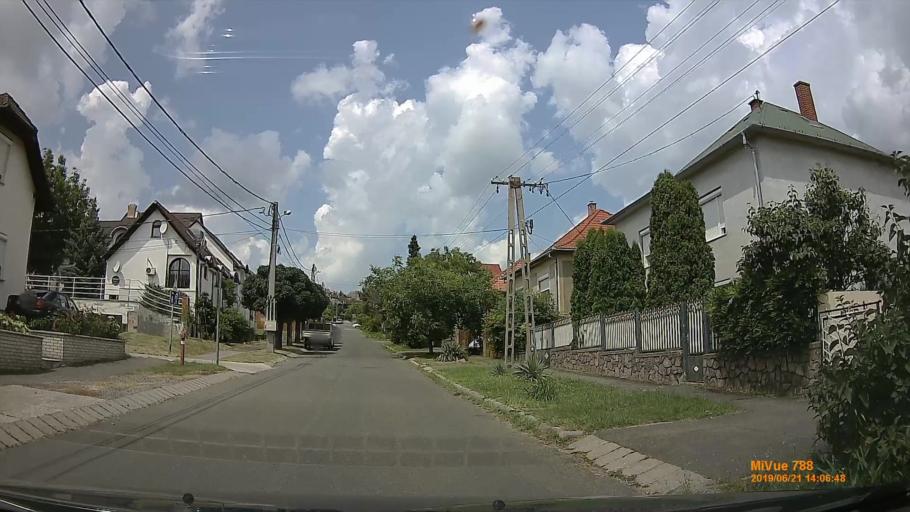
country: HU
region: Baranya
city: Pellerd
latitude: 46.0668
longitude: 18.1697
